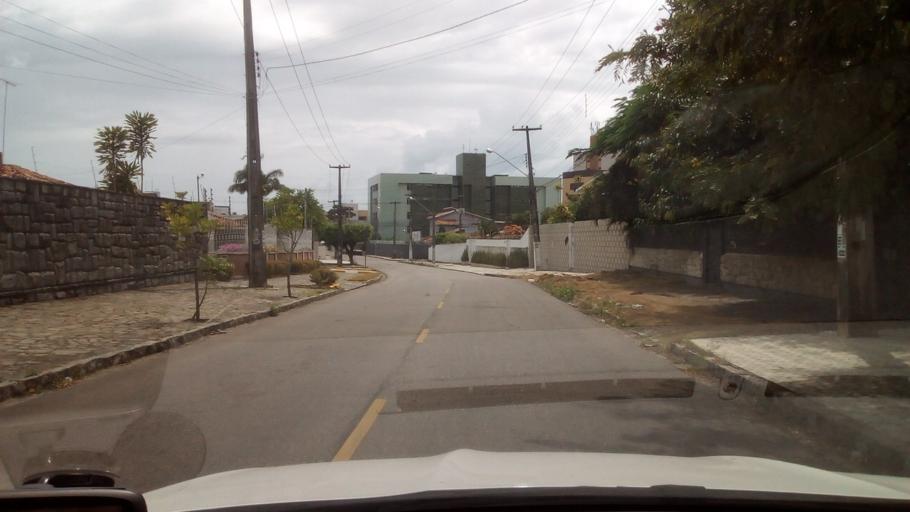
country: BR
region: Paraiba
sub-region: Joao Pessoa
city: Joao Pessoa
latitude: -7.1307
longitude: -34.8622
